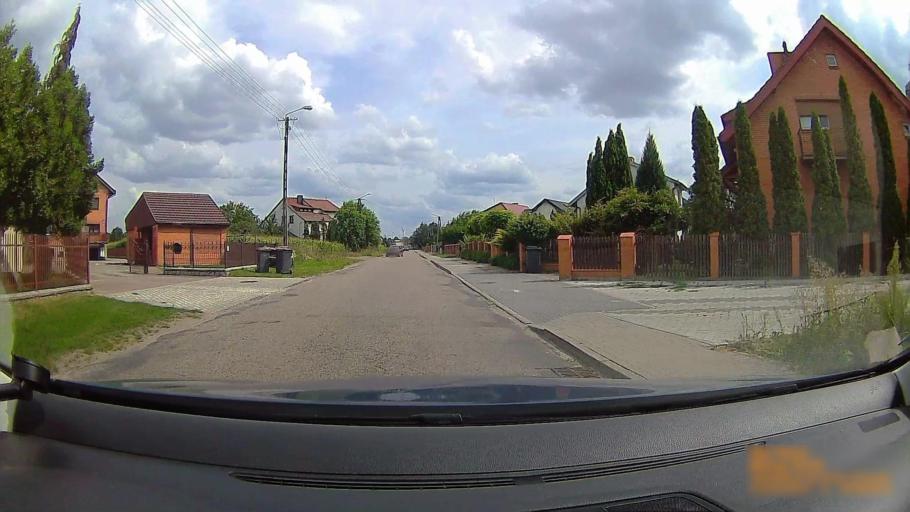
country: PL
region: Greater Poland Voivodeship
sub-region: Powiat koninski
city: Rychwal
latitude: 52.0739
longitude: 18.1541
